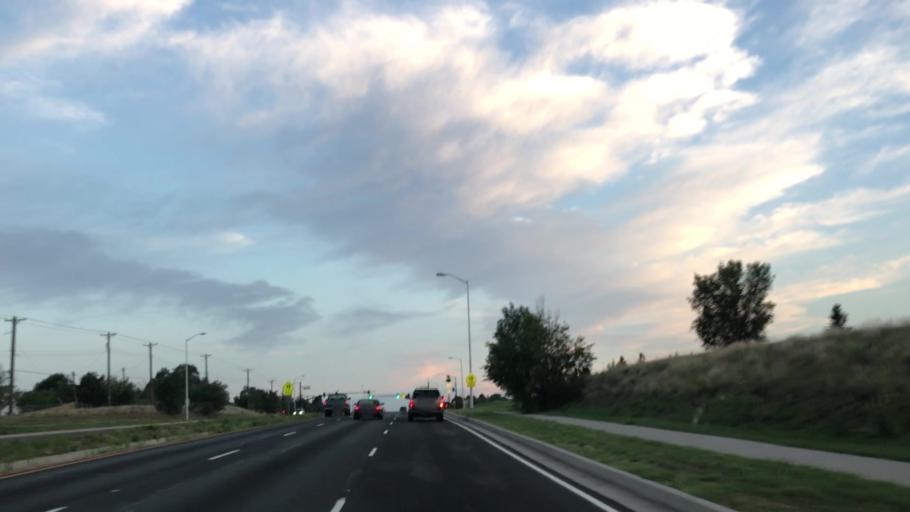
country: US
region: Colorado
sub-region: El Paso County
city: Stratmoor
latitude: 38.8129
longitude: -104.7803
